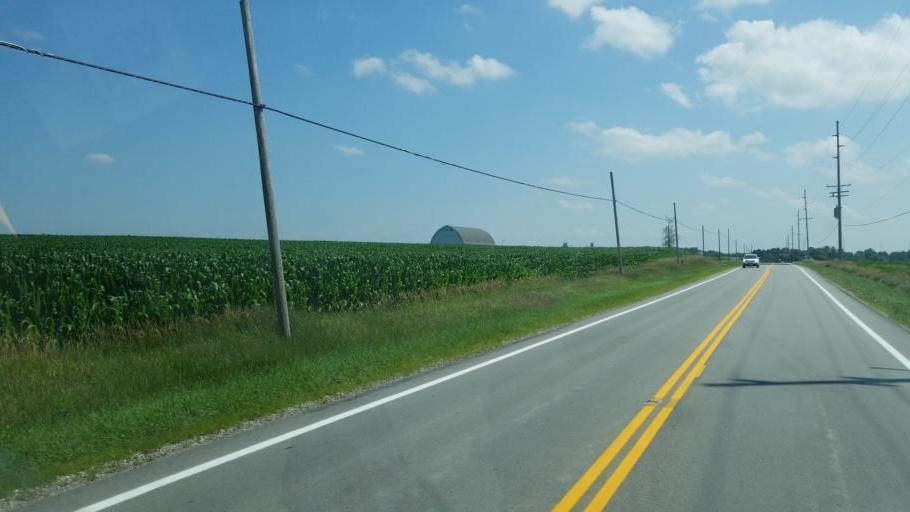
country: US
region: Ohio
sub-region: Huron County
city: Bellevue
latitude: 41.3100
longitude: -82.8294
